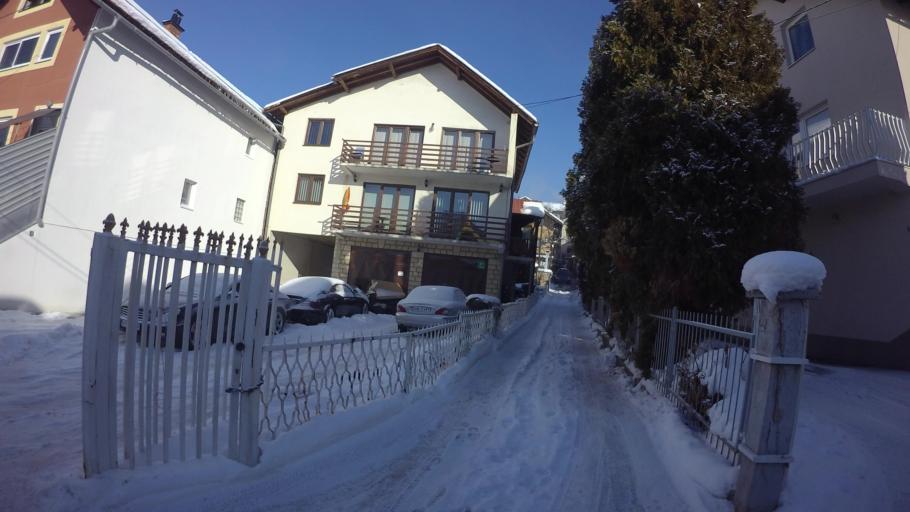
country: BA
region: Federation of Bosnia and Herzegovina
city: Kobilja Glava
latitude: 43.8813
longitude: 18.4173
